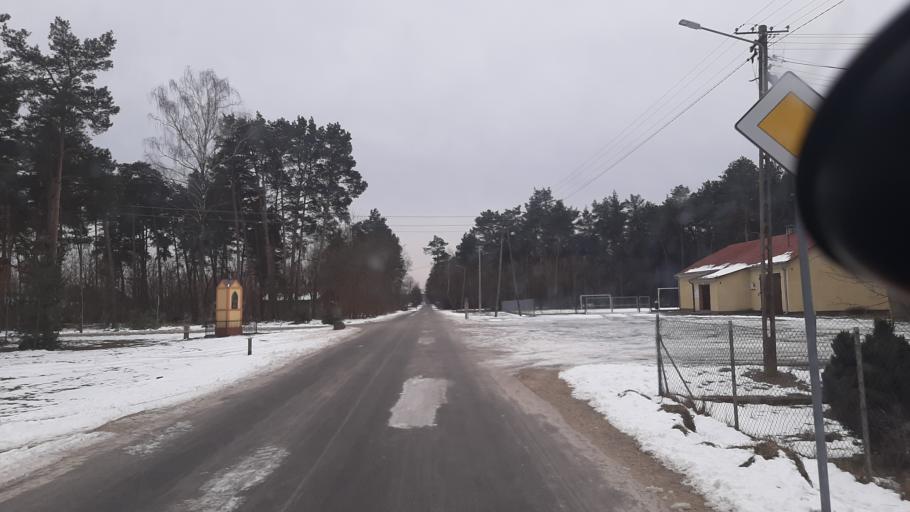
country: PL
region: Lublin Voivodeship
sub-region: Powiat lubartowski
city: Kamionka
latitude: 51.5037
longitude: 22.4542
